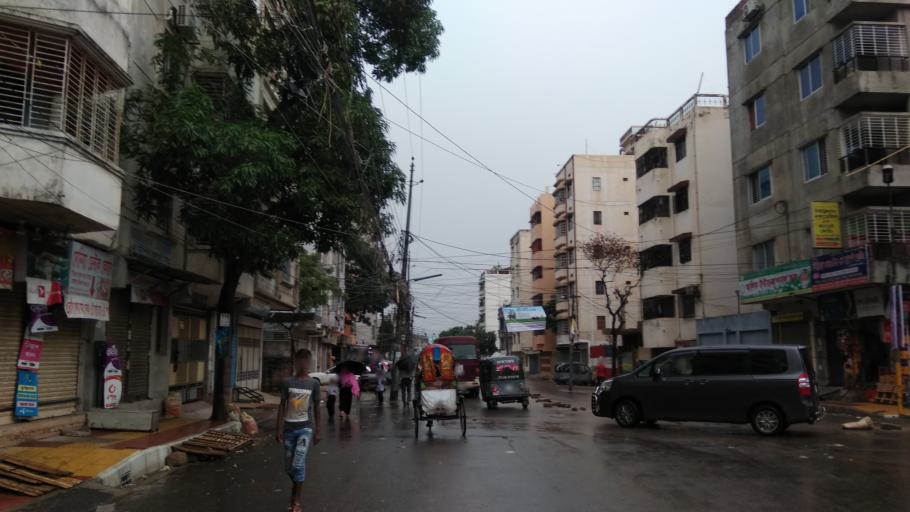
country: BD
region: Dhaka
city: Tungi
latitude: 23.8270
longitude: 90.3732
